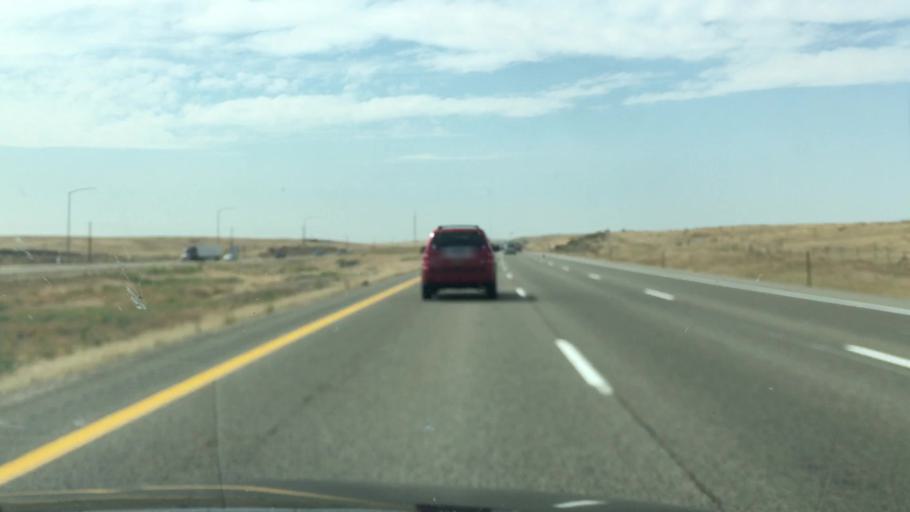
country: US
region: Idaho
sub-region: Ada County
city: Boise
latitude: 43.4357
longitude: -116.0622
